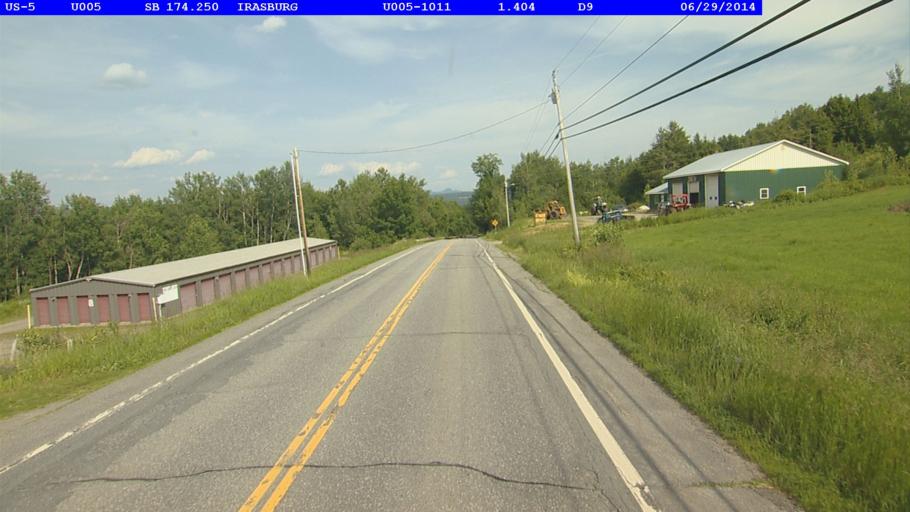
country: US
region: Vermont
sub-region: Orleans County
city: Newport
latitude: 44.8231
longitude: -72.2297
